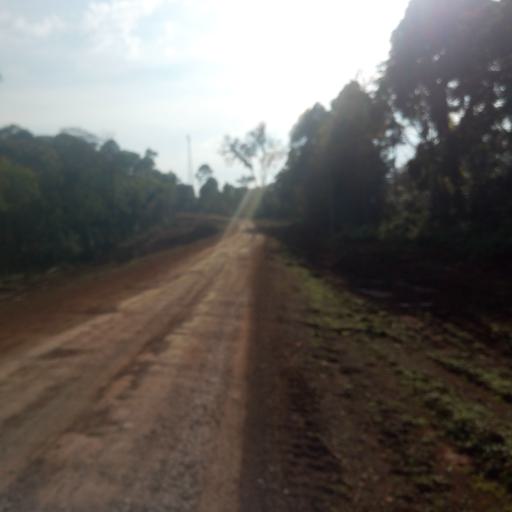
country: ET
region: Oromiya
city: Gore
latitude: 7.9023
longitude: 35.5004
